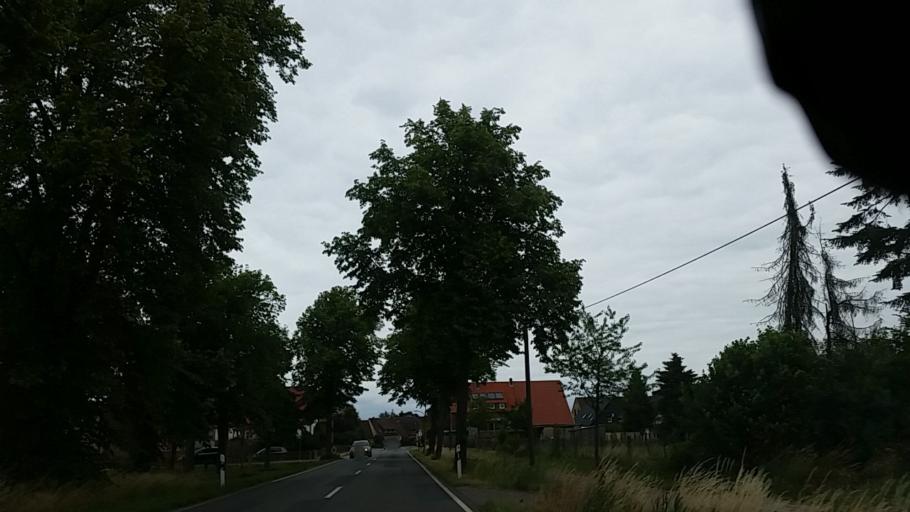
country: DE
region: Lower Saxony
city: Grafhorst
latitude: 52.4428
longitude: 10.9398
